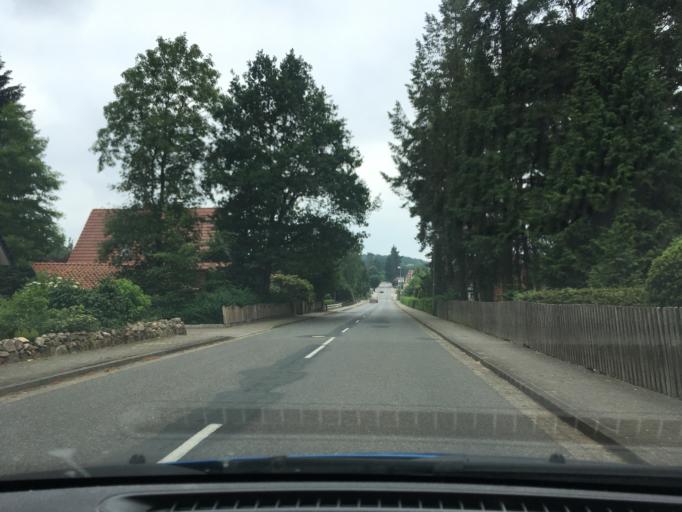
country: DE
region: Lower Saxony
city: Zernien
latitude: 53.0719
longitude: 10.8839
